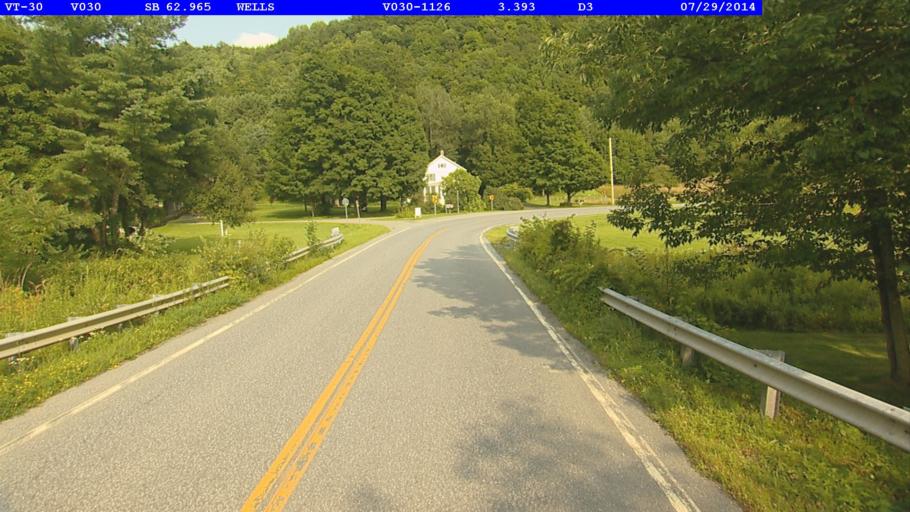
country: US
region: New York
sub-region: Washington County
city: Granville
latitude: 43.4422
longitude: -73.1965
